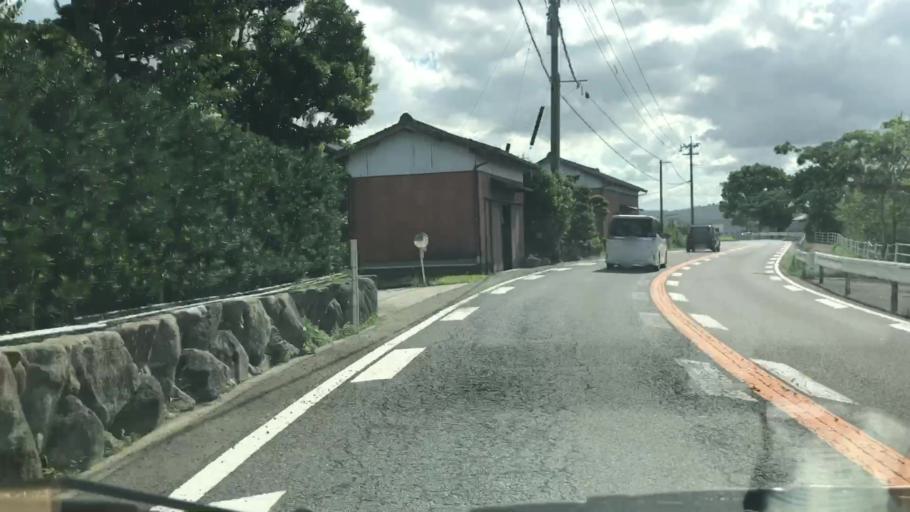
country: JP
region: Saga Prefecture
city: Kashima
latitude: 33.1651
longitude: 130.1692
